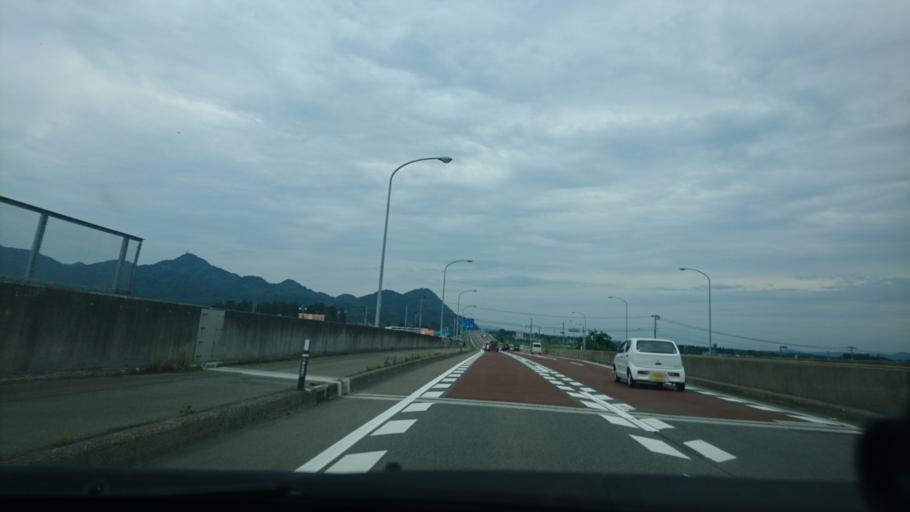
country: JP
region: Akita
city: Omagari
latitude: 39.4744
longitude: 140.4781
